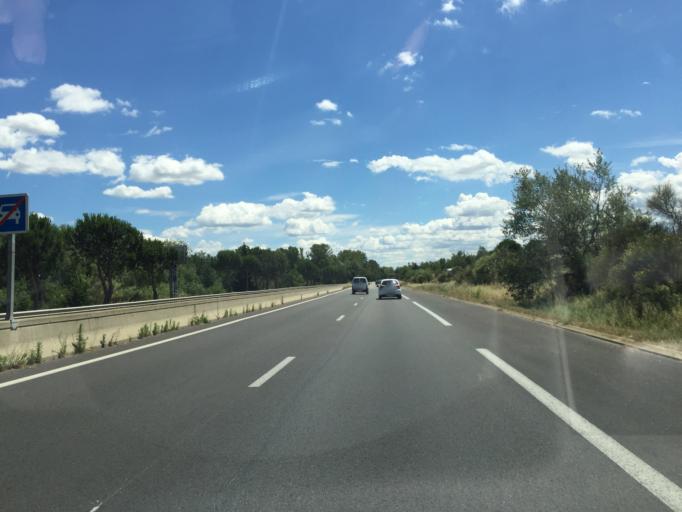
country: FR
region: Provence-Alpes-Cote d'Azur
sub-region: Departement du Vaucluse
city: Sorgues
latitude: 44.0029
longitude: 4.8638
